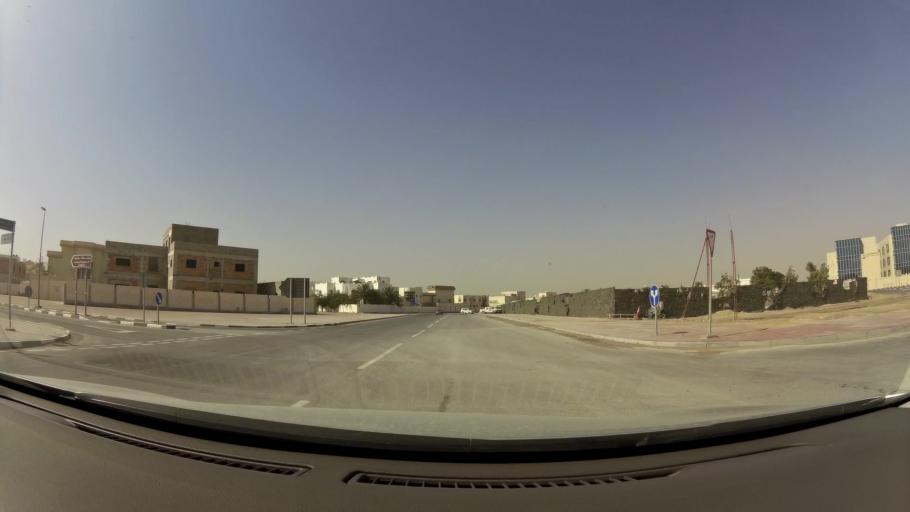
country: QA
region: Baladiyat ad Dawhah
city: Doha
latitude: 25.3572
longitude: 51.5185
